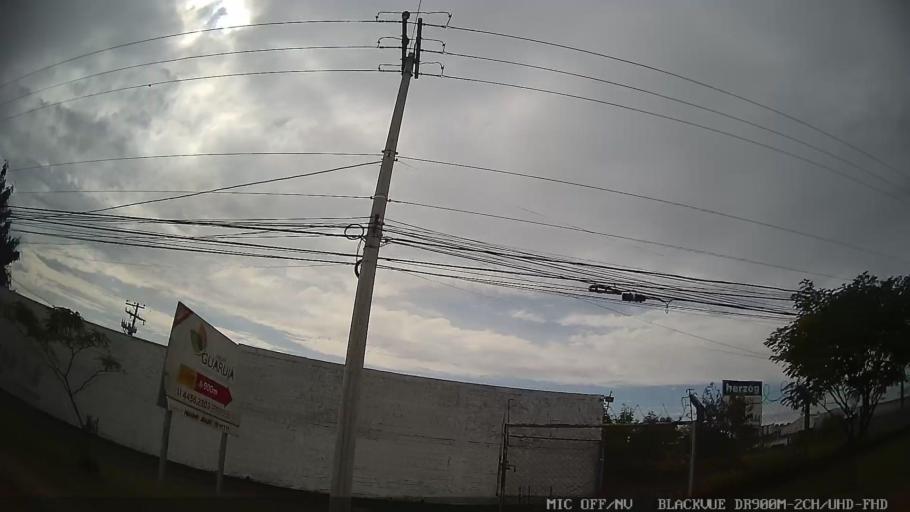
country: BR
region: Sao Paulo
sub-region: Salto
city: Salto
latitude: -23.2150
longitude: -47.2701
